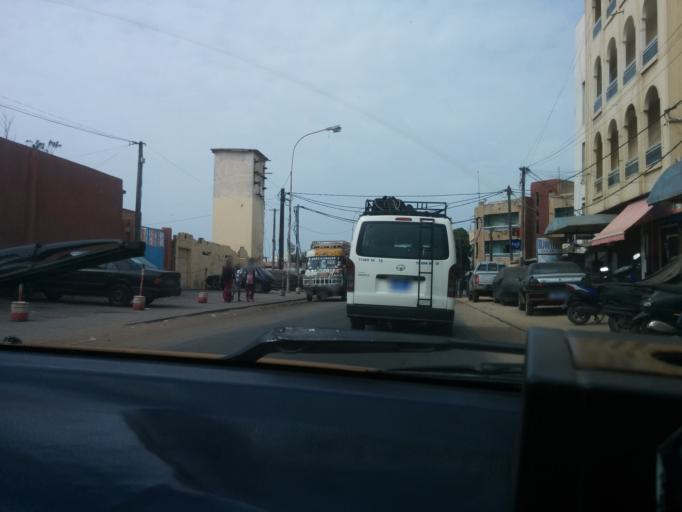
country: SN
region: Dakar
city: Pikine
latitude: 14.7589
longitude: -17.4364
